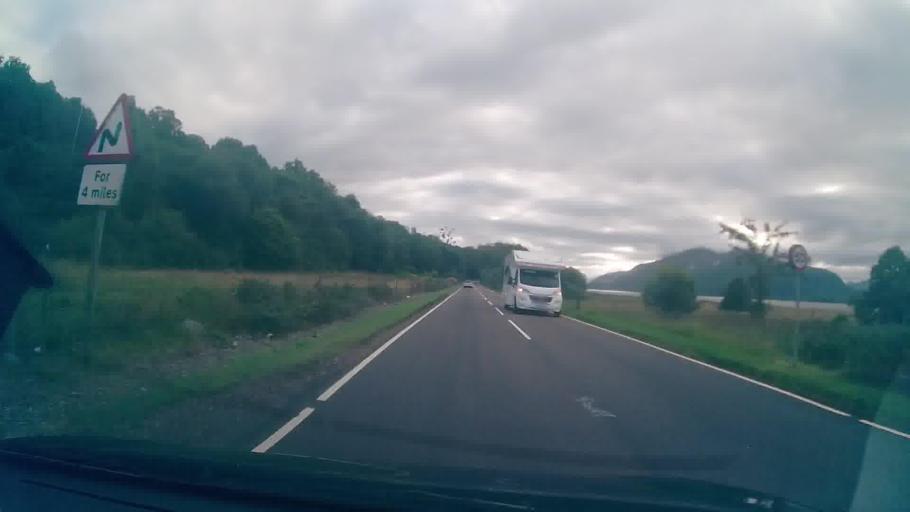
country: GB
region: Scotland
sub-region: Highland
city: Fort William
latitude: 56.7720
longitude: -5.1675
